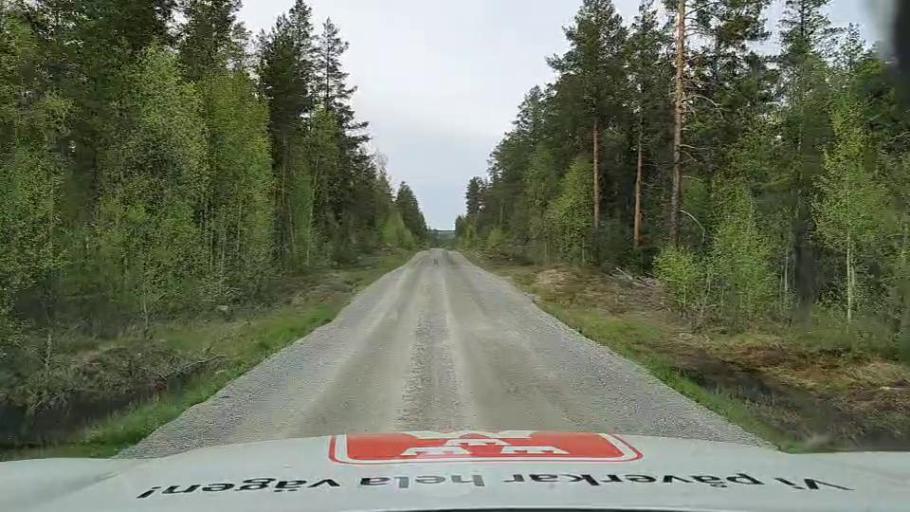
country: SE
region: Jaemtland
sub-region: Braecke Kommun
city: Braecke
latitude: 62.4770
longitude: 14.9169
